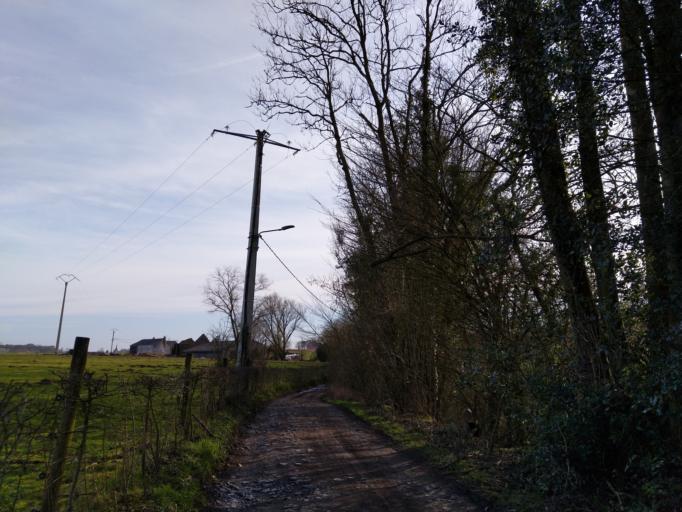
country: BE
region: Wallonia
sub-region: Province du Hainaut
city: Soignies
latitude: 50.5089
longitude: 4.0248
